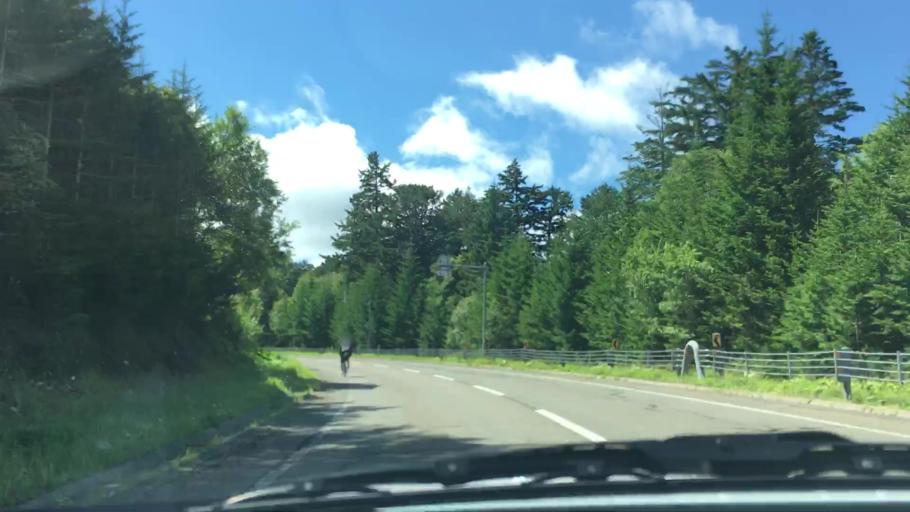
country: JP
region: Hokkaido
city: Kitami
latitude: 43.4429
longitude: 144.0131
